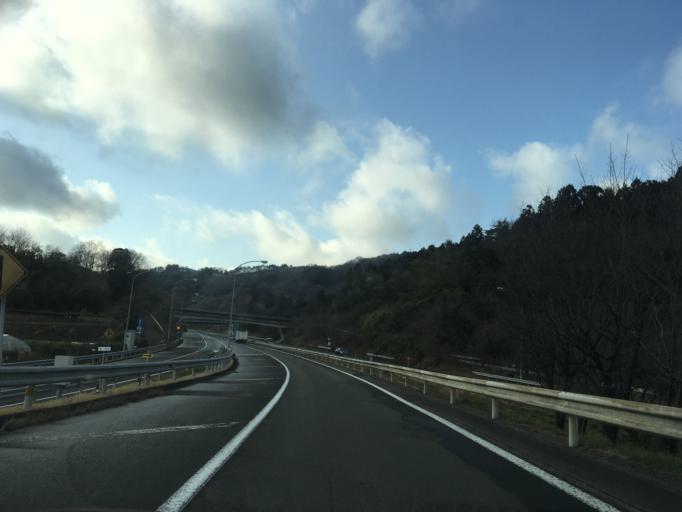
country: JP
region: Miyagi
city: Okawara
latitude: 38.1407
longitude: 140.7223
